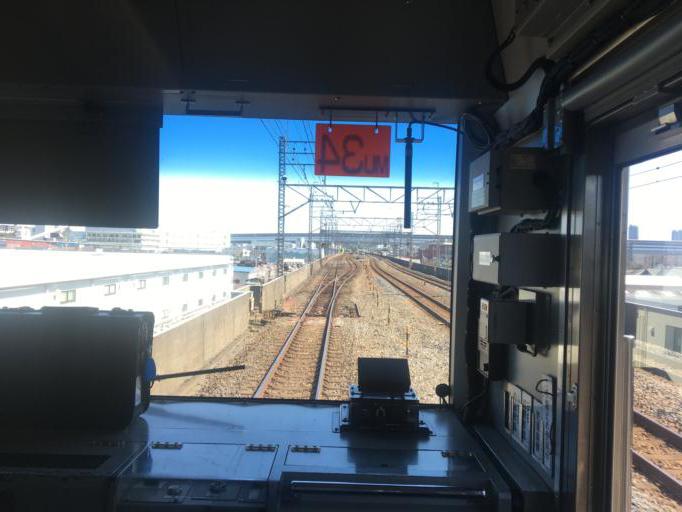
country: JP
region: Saitama
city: Shiki
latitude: 35.8409
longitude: 139.6226
